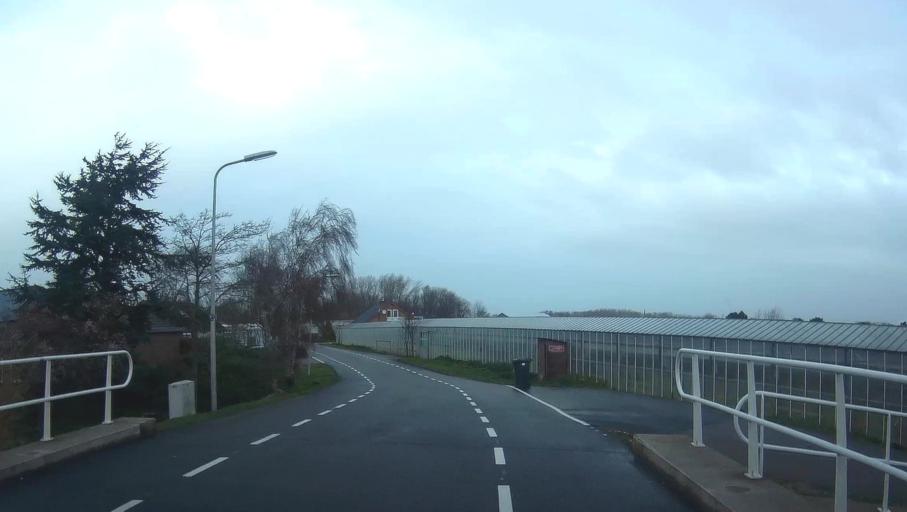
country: NL
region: South Holland
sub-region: Gemeente Westland
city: Poeldijk
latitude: 52.0309
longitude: 4.2066
